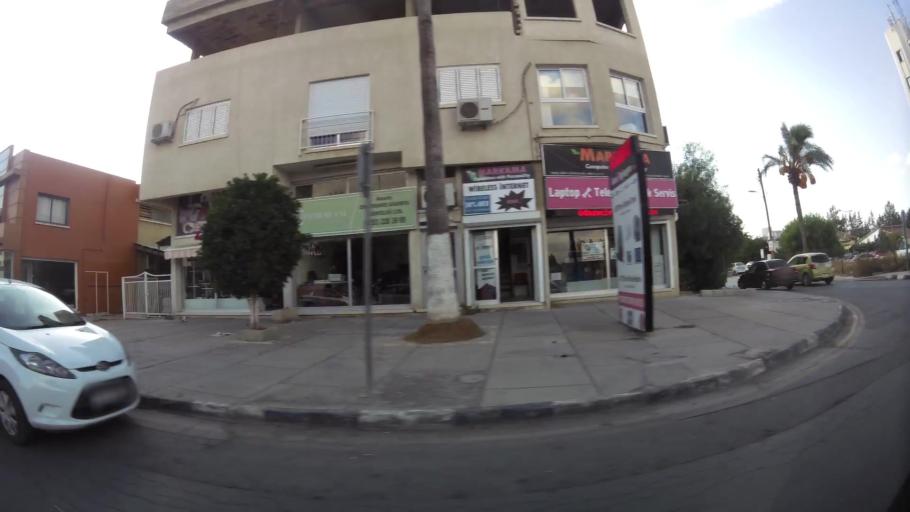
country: CY
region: Lefkosia
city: Nicosia
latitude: 35.1994
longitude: 33.3675
